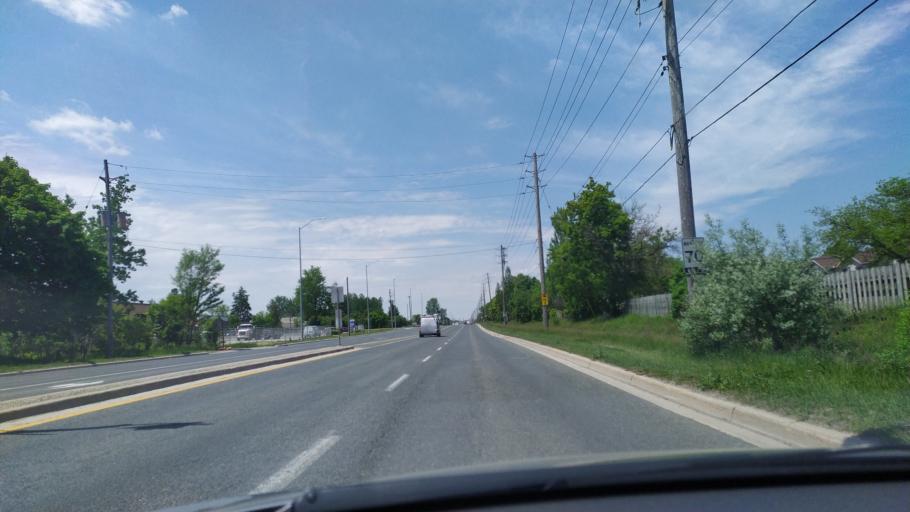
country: CA
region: Ontario
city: London
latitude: 42.9246
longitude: -81.2321
